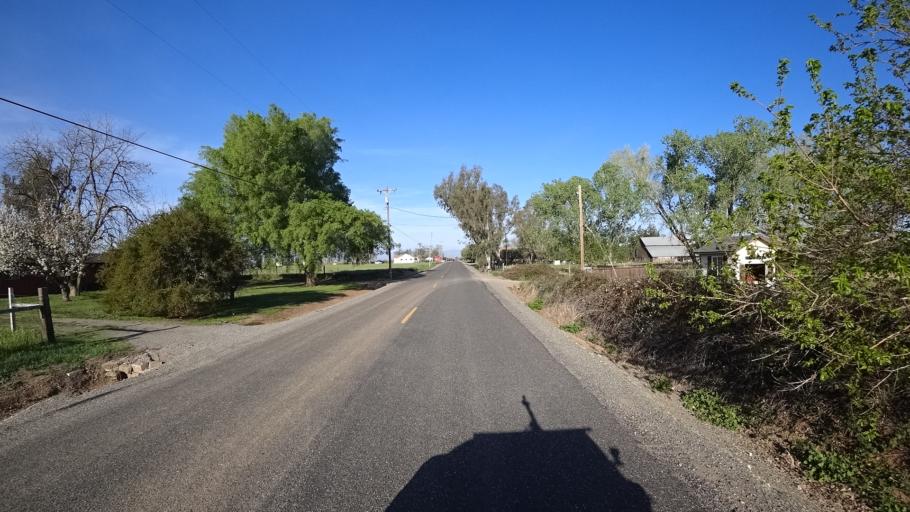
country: US
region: California
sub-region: Glenn County
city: Orland
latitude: 39.7260
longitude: -122.2248
